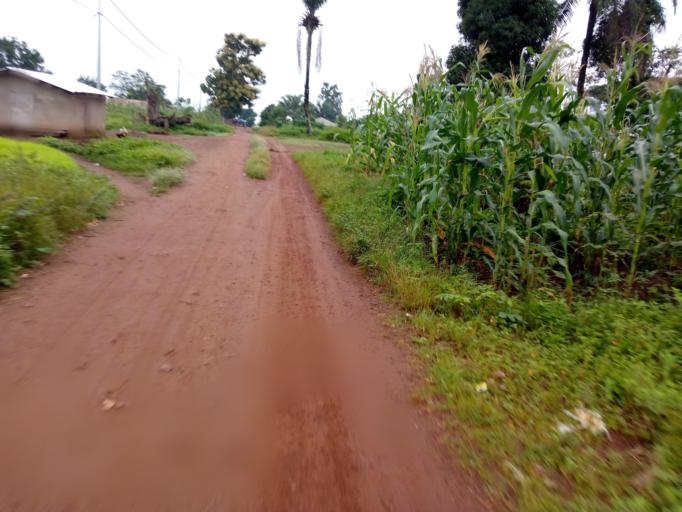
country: SL
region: Eastern Province
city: Buedu
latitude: 8.4658
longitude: -10.3426
